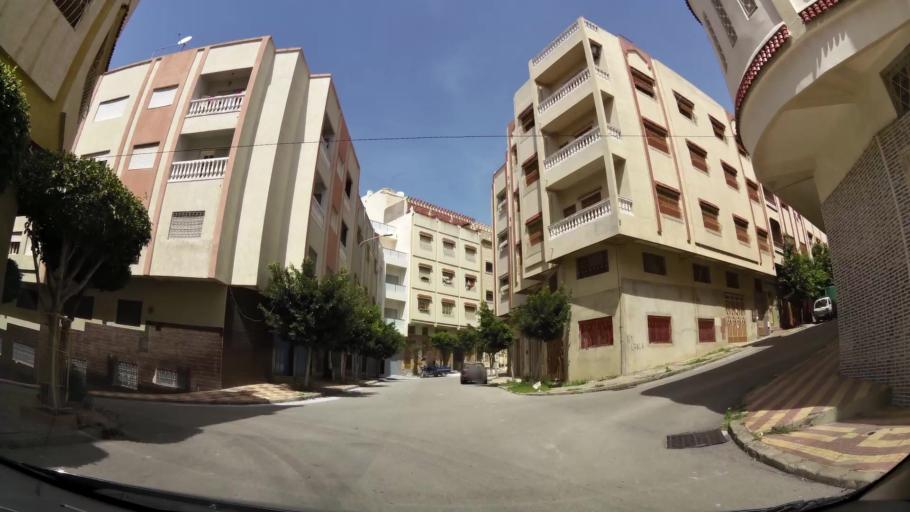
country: MA
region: Tanger-Tetouan
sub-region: Tanger-Assilah
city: Tangier
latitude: 35.7599
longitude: -5.8397
